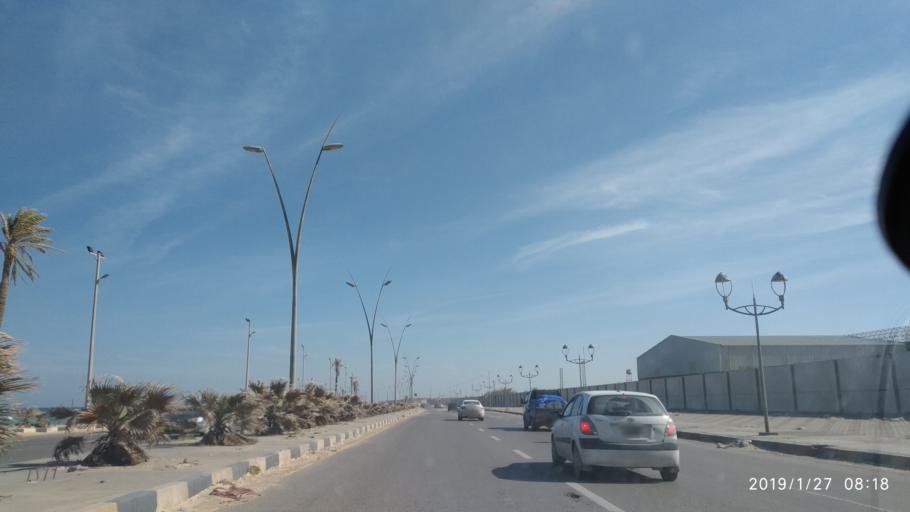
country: LY
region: Tripoli
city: Tagiura
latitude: 32.9084
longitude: 13.2791
